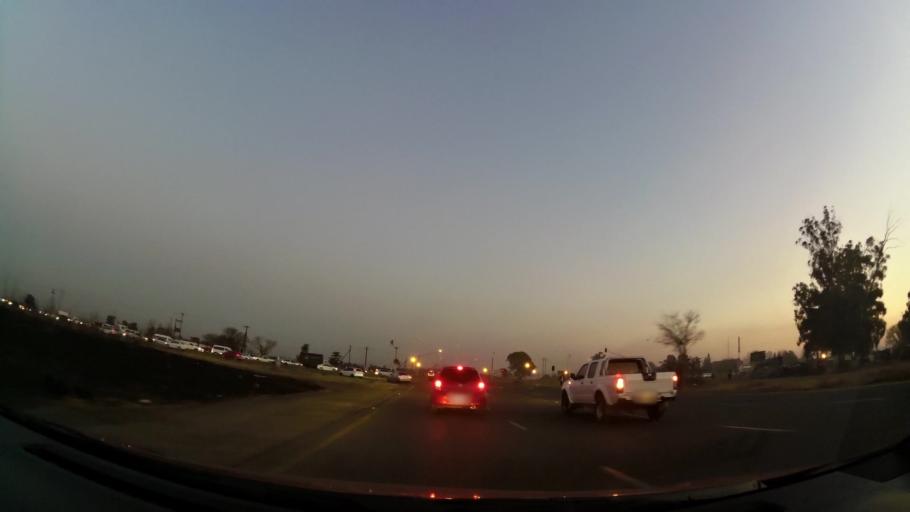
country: ZA
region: Gauteng
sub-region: City of Johannesburg Metropolitan Municipality
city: Soweto
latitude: -26.2984
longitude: 27.8158
